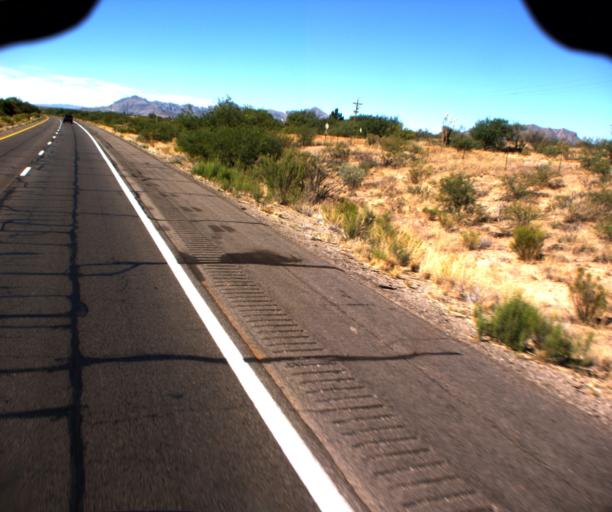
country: US
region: Arizona
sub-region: Pima County
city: Arivaca Junction
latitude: 31.7040
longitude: -111.0656
